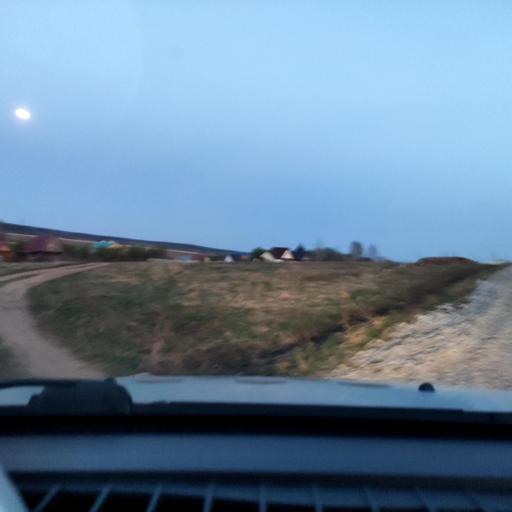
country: RU
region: Perm
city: Ferma
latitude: 57.9398
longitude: 56.3441
